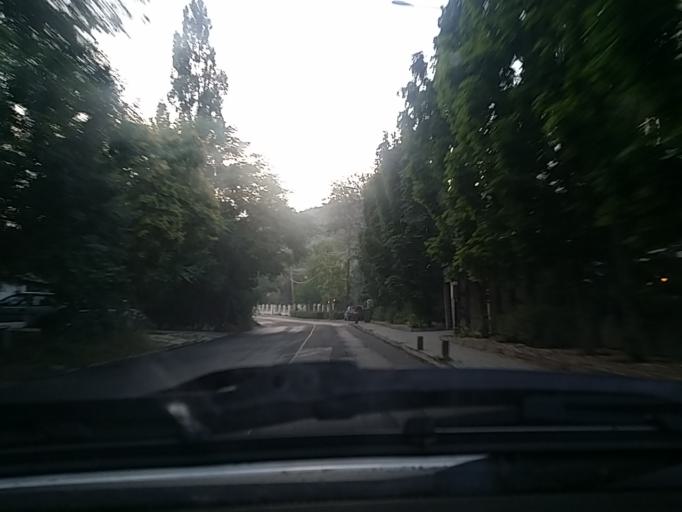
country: HU
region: Budapest
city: Budapest II. keruelet
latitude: 47.5361
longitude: 19.0151
